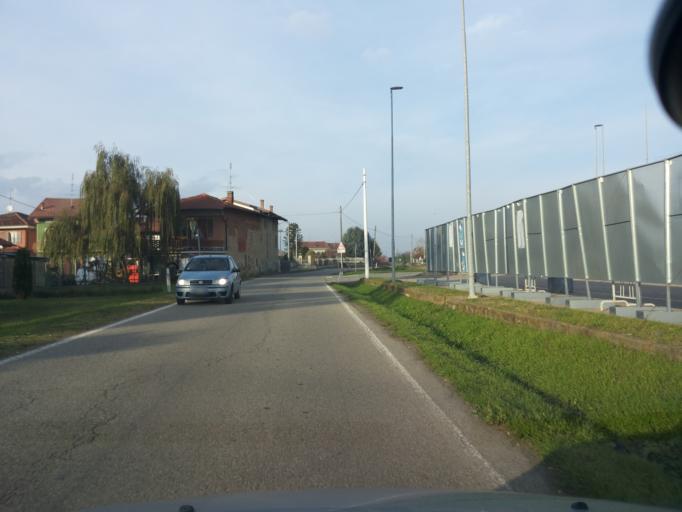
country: IT
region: Piedmont
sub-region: Provincia di Biella
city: Salussola
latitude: 45.4608
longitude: 8.1157
